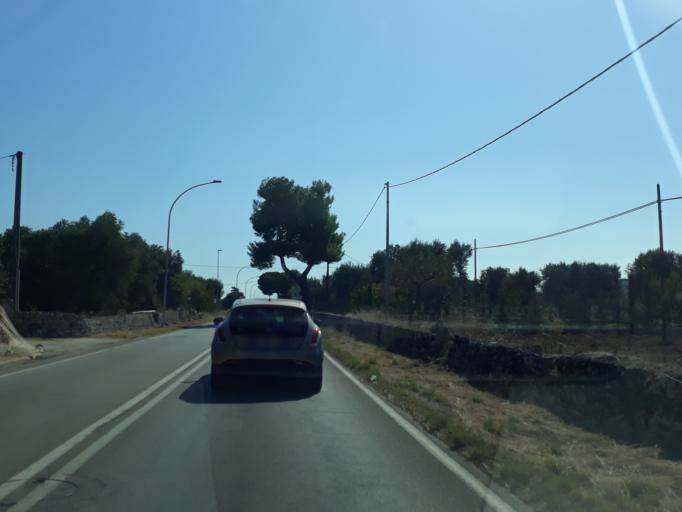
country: IT
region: Apulia
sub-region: Provincia di Bari
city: Monopoli
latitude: 40.9318
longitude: 17.3113
